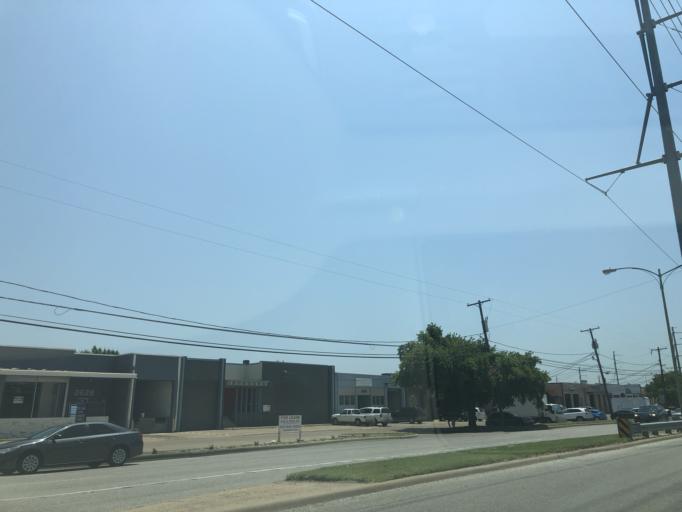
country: US
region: Texas
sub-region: Dallas County
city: Dallas
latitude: 32.8016
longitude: -96.8429
